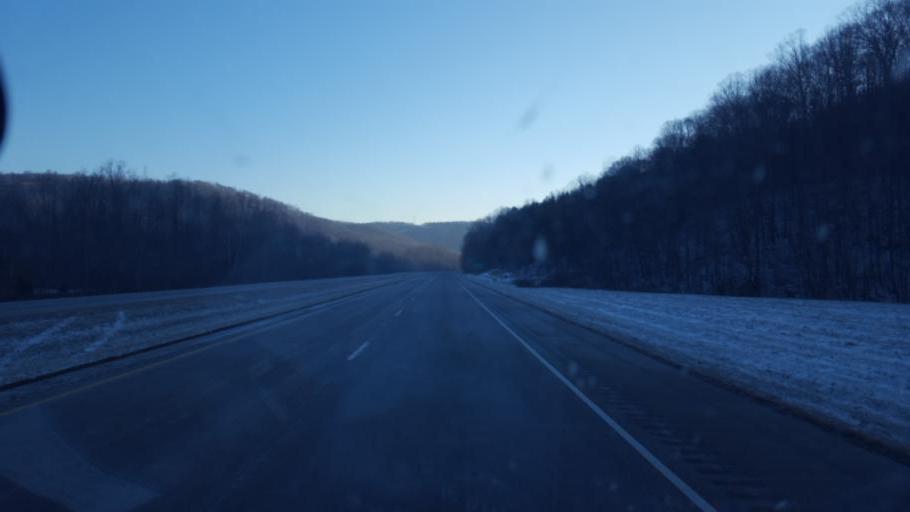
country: US
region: Ohio
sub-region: Pike County
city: Piketon
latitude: 39.0505
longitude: -83.2024
